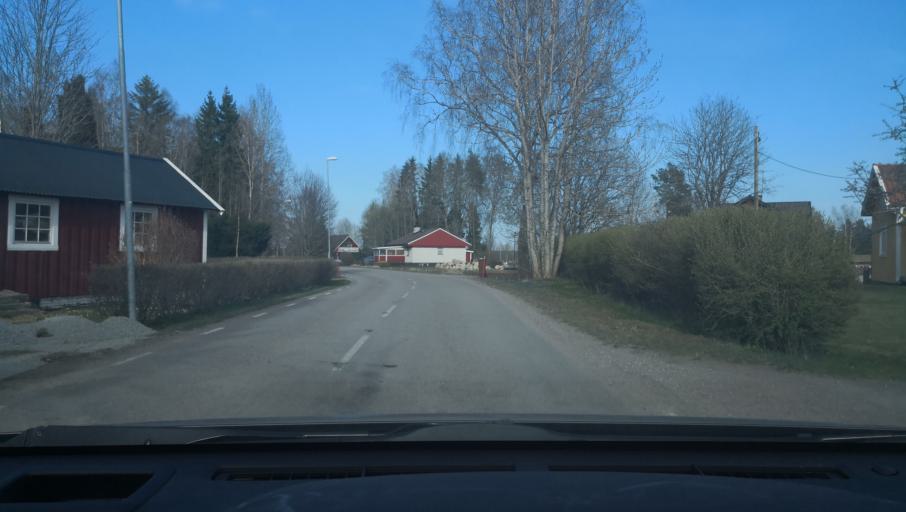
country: SE
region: Uppsala
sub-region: Heby Kommun
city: Heby
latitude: 59.9232
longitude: 16.8508
